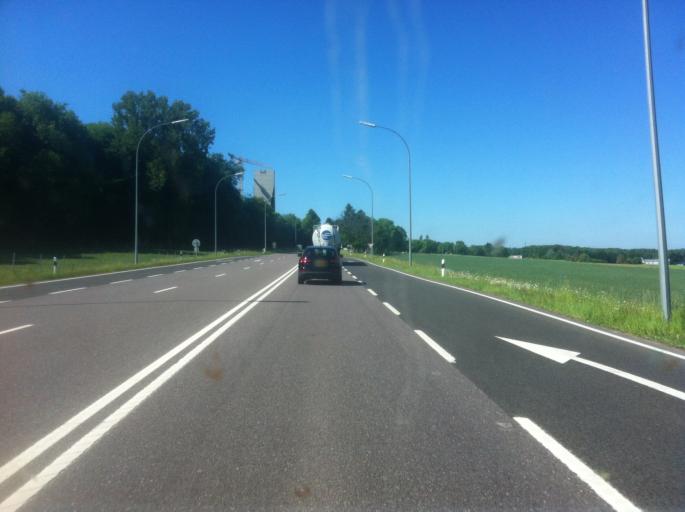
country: LU
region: Grevenmacher
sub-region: Canton d'Echternach
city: Consdorf
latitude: 49.7560
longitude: 6.3384
